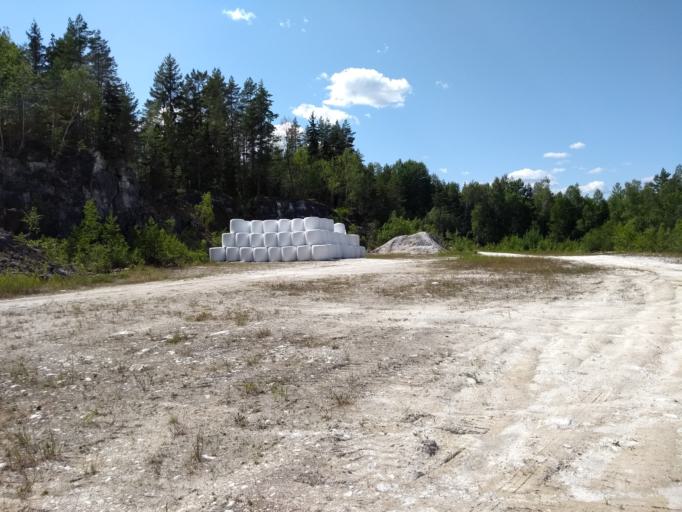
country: SE
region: OEstergoetland
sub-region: Norrkopings Kommun
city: Krokek
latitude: 58.8250
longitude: 16.3226
